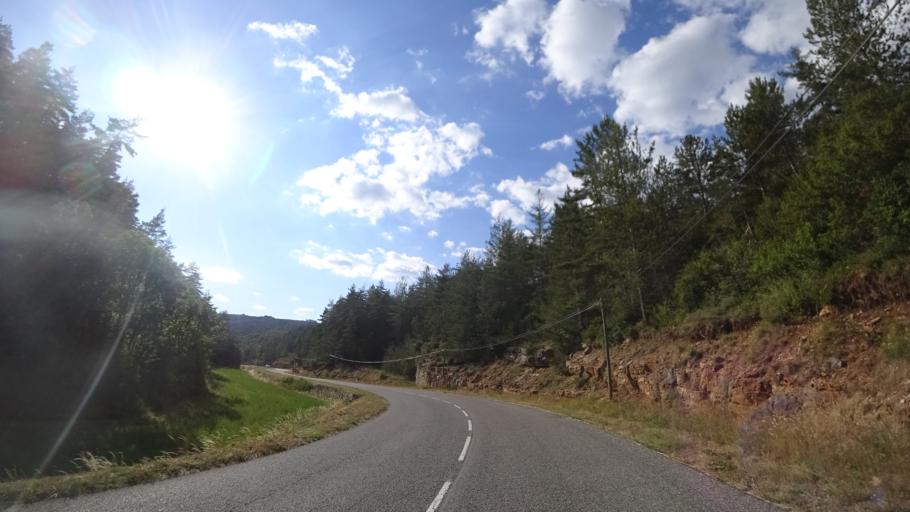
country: FR
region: Languedoc-Roussillon
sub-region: Departement de la Lozere
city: La Canourgue
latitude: 44.4094
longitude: 3.2760
